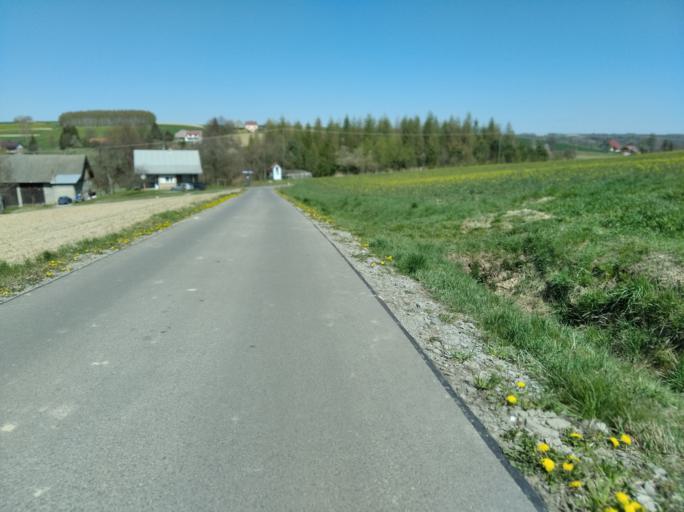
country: PL
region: Subcarpathian Voivodeship
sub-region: Powiat strzyzowski
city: Wisniowa
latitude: 49.9077
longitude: 21.6869
